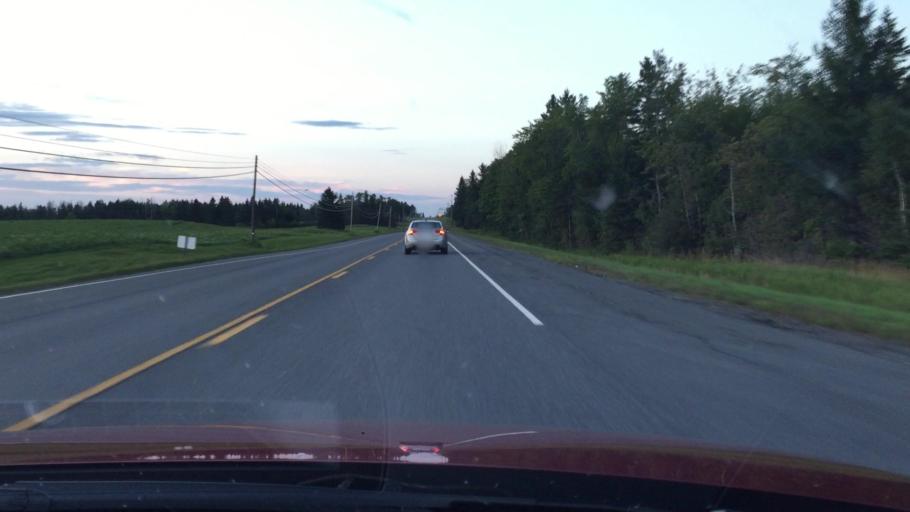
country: US
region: Maine
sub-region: Aroostook County
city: Easton
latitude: 46.4814
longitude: -67.8684
